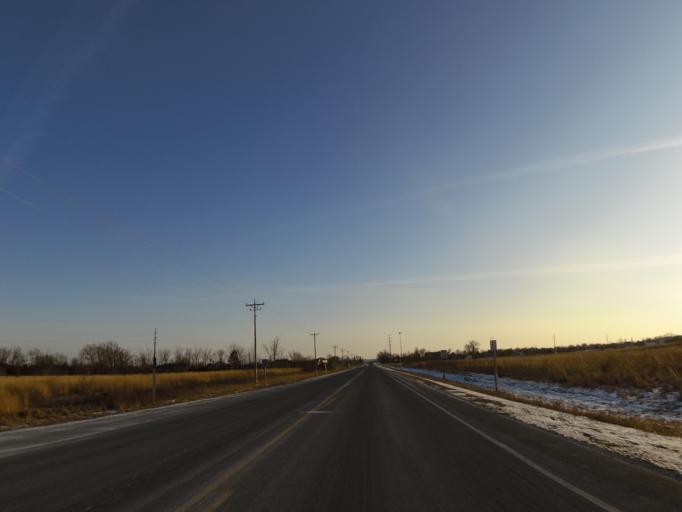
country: US
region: Wisconsin
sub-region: Saint Croix County
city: North Hudson
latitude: 45.0124
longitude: -92.6756
